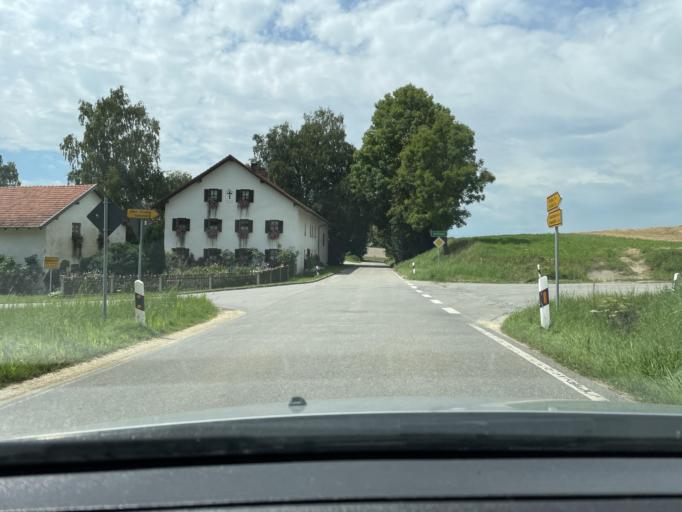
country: DE
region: Bavaria
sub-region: Lower Bavaria
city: Geisenhausen
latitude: 48.4366
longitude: 12.2853
